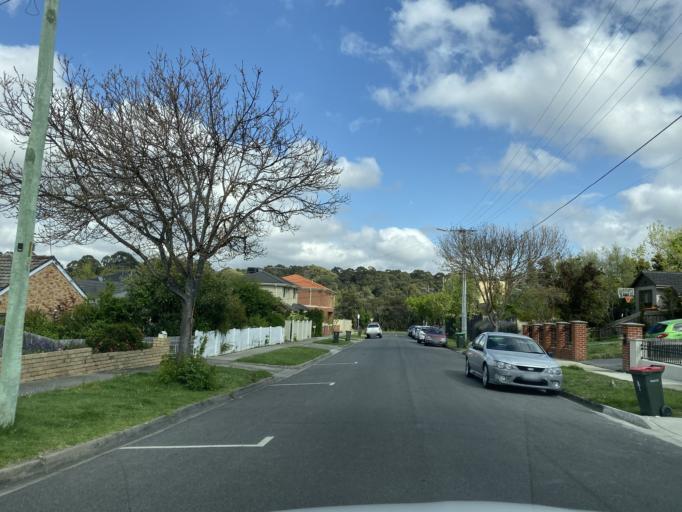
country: AU
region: Victoria
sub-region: Whitehorse
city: Box Hill South
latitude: -37.8397
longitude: 145.1121
